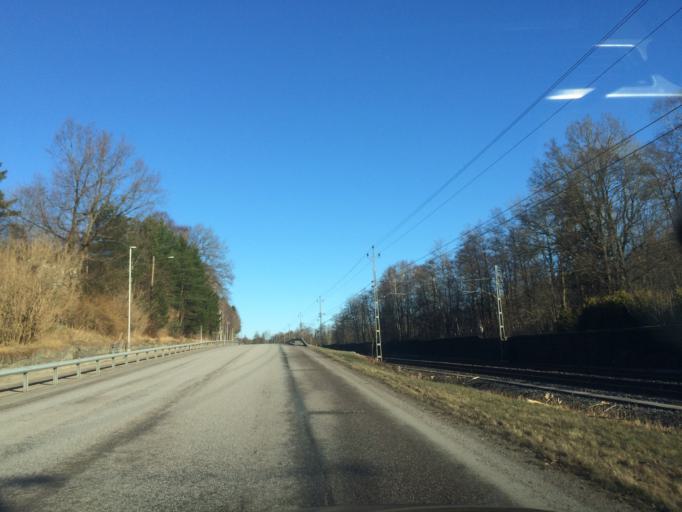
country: SE
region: Vaestra Goetaland
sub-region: Molndal
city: Lindome
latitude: 57.5813
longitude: 12.0754
